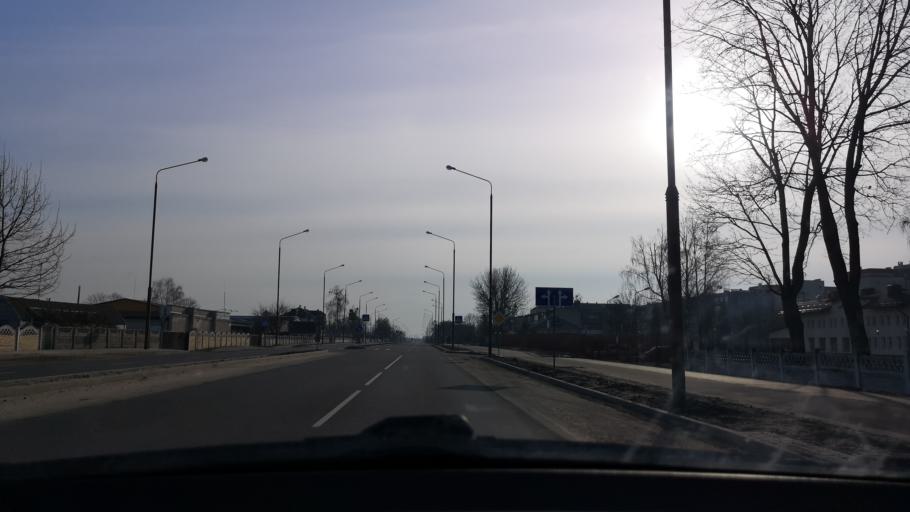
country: BY
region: Brest
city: Brest
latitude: 52.1223
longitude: 23.6713
